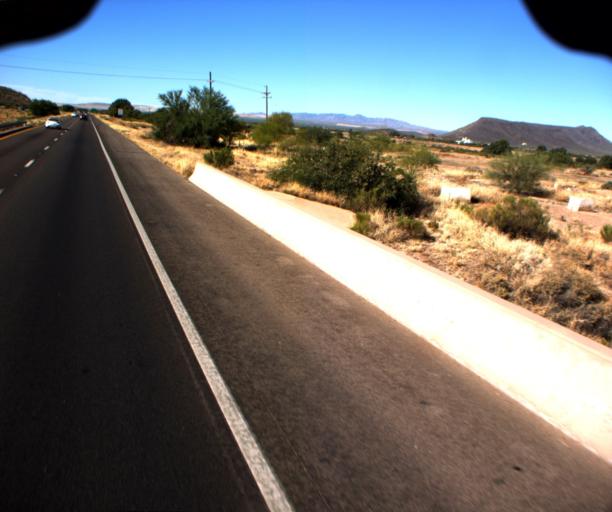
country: US
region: Arizona
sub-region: Pima County
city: Drexel Heights
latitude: 32.1203
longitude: -110.9889
